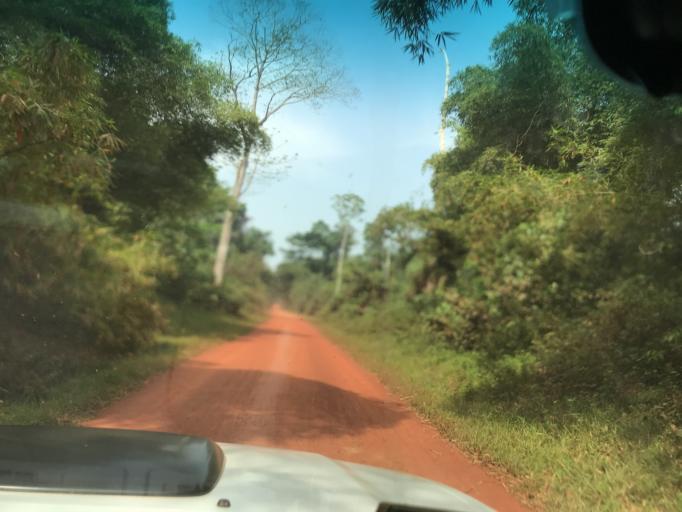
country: CD
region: Eastern Province
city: Buta
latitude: 2.8956
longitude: 24.3258
